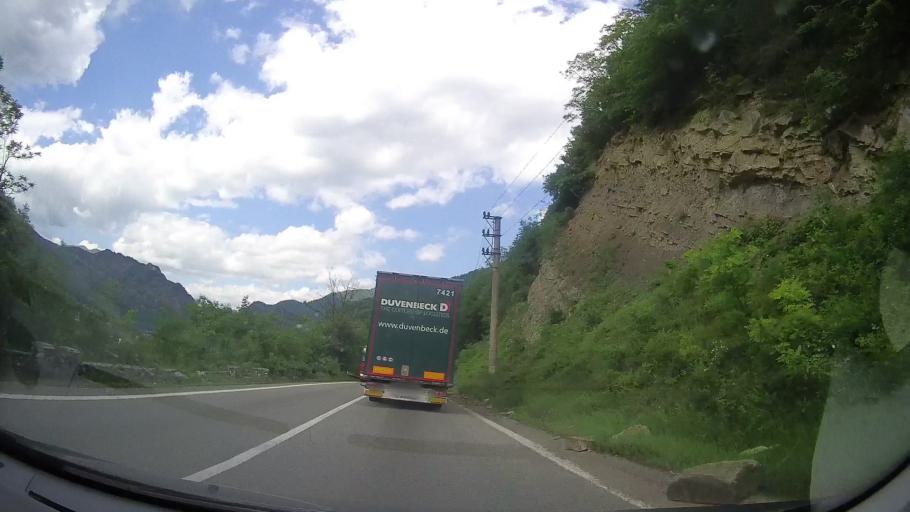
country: RO
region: Valcea
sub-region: Oras Calimanesti
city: Calimanesti
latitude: 45.2671
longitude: 24.3230
